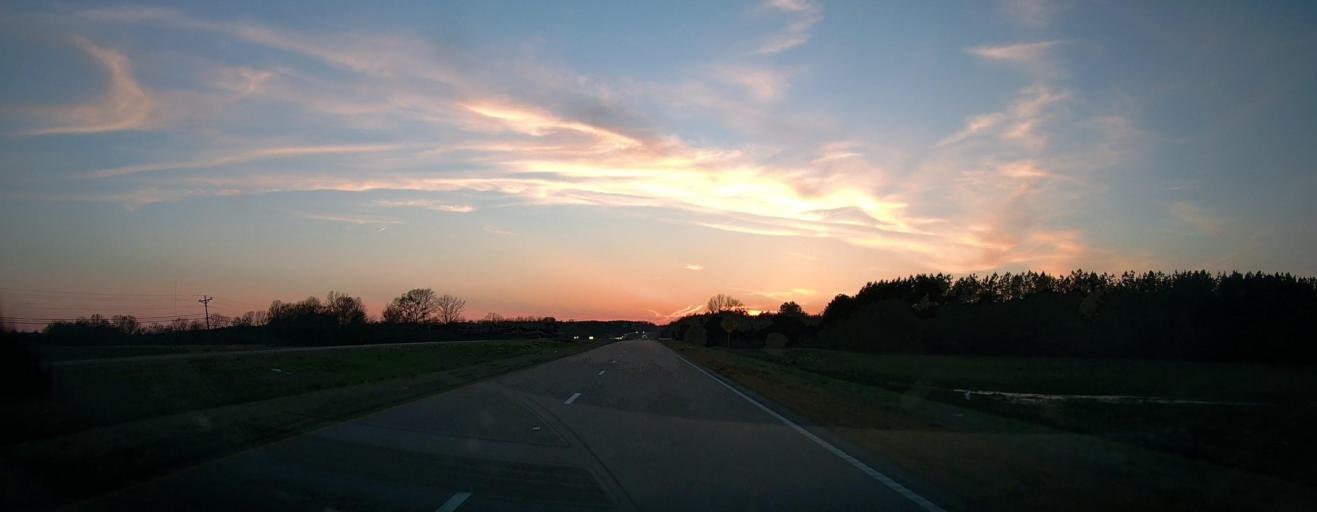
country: US
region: Mississippi
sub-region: Tippah County
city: Ripley
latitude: 34.9543
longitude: -88.8689
